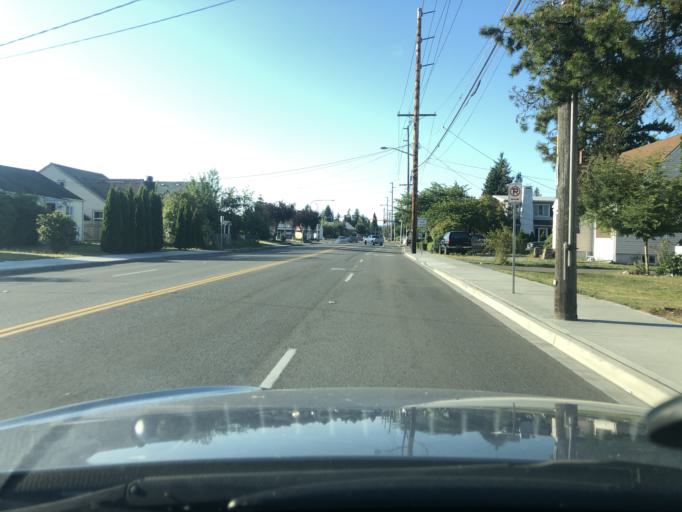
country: US
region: Washington
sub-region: King County
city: Auburn
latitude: 47.3066
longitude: -122.2134
